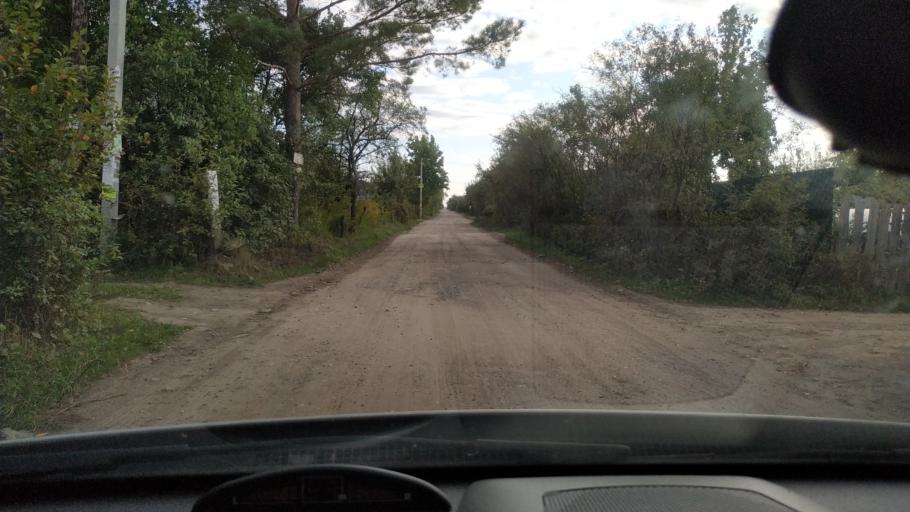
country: RU
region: Rjazan
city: Polyany
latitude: 54.5582
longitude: 39.8769
